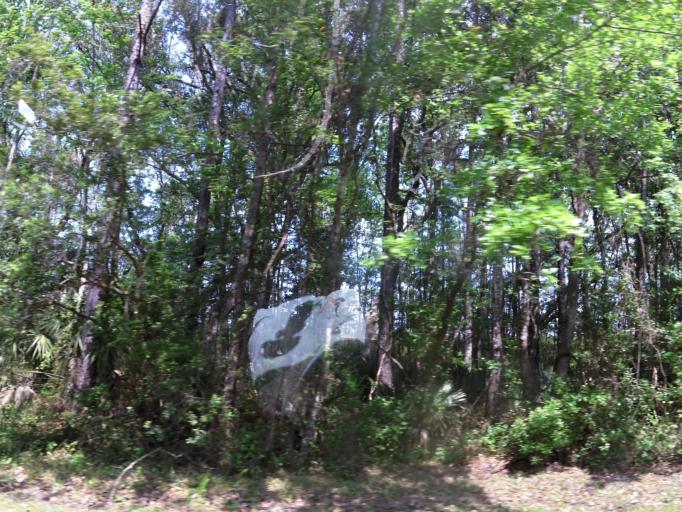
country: US
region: Georgia
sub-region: Camden County
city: Kingsland
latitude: 30.7943
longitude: -81.7185
